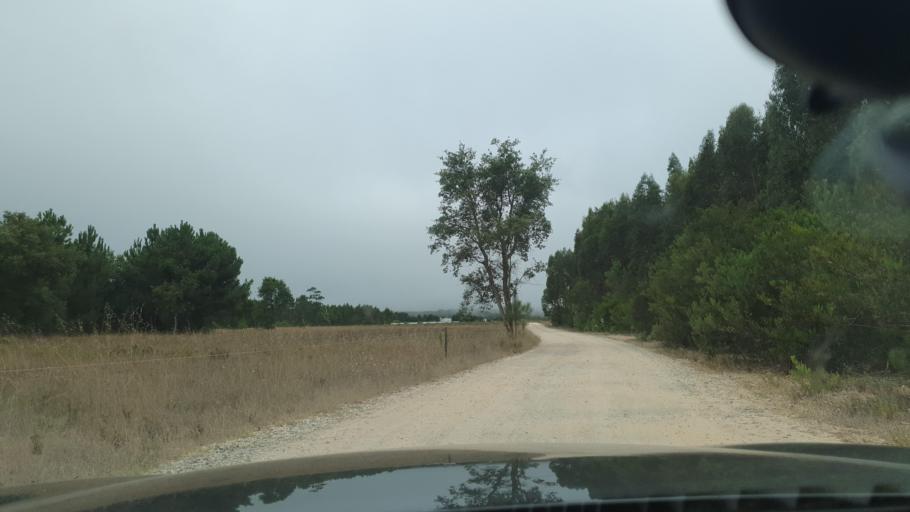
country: PT
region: Beja
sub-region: Odemira
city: Sao Teotonio
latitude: 37.4967
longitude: -8.6818
